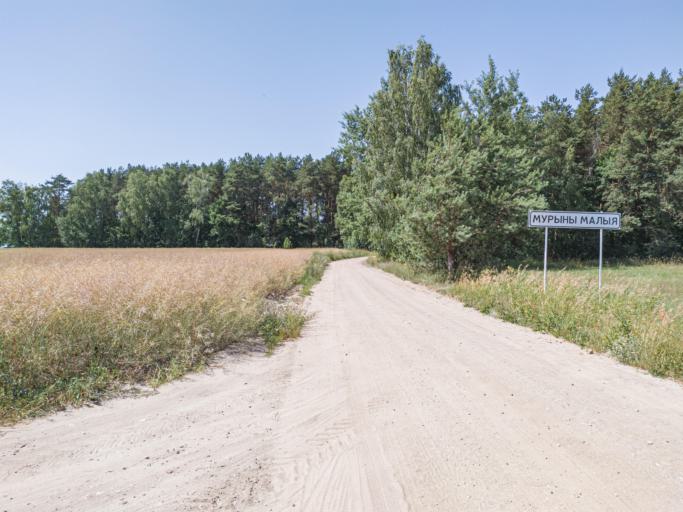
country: BY
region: Brest
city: Kamyanyets
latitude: 52.3829
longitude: 23.7838
